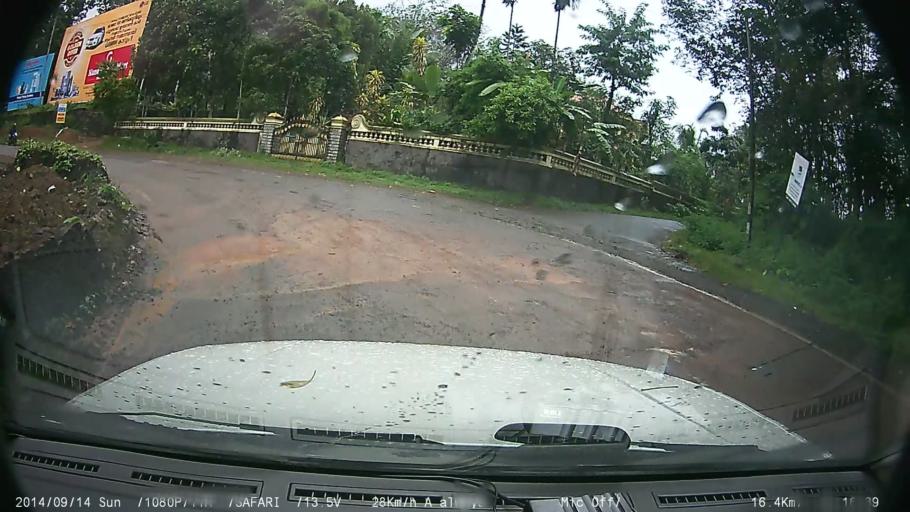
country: IN
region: Kerala
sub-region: Kottayam
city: Palackattumala
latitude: 9.7056
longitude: 76.5549
